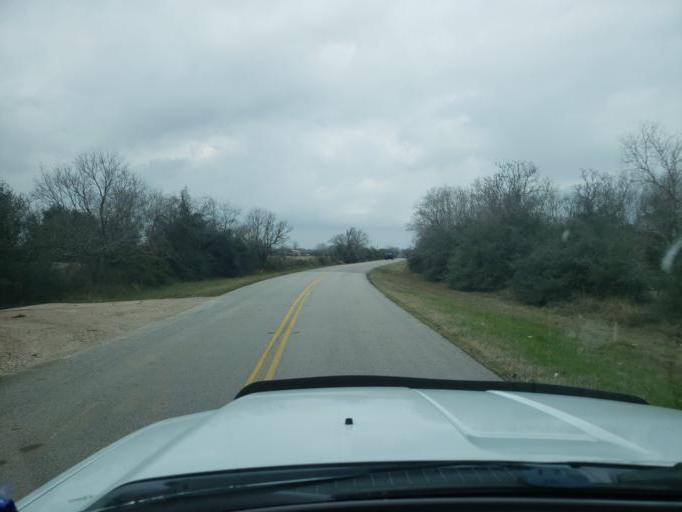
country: US
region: Texas
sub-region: Fort Bend County
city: Needville
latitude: 29.3708
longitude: -95.7309
